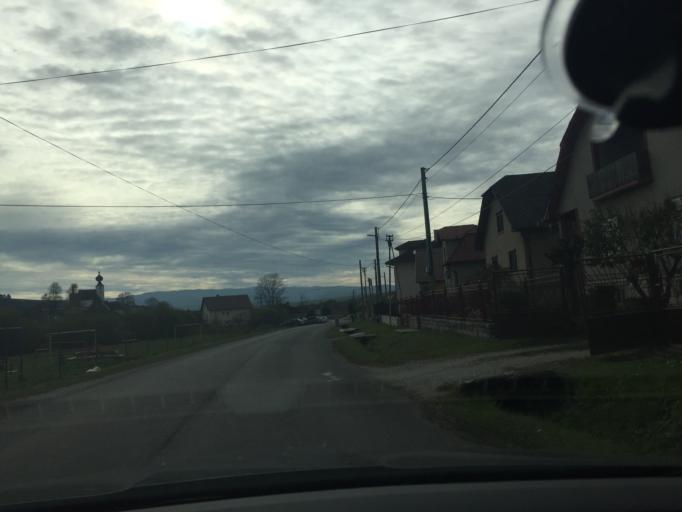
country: SK
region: Presovsky
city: Spisske Podhradie
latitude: 48.9832
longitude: 20.7936
